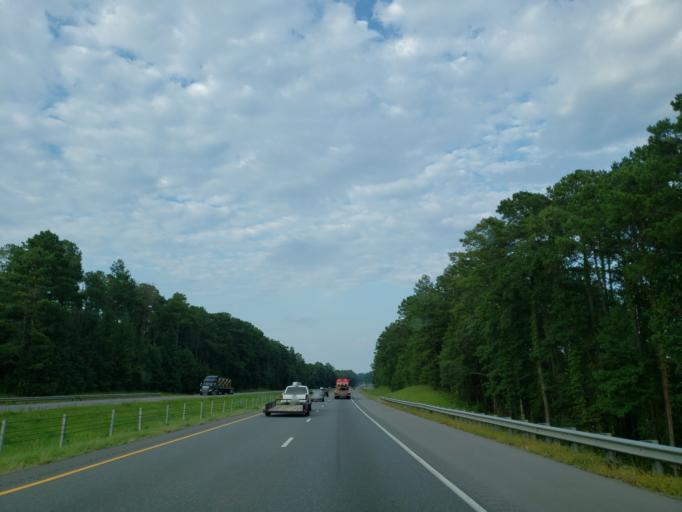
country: US
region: Alabama
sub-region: Greene County
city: Eutaw
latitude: 32.9588
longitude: -87.8281
